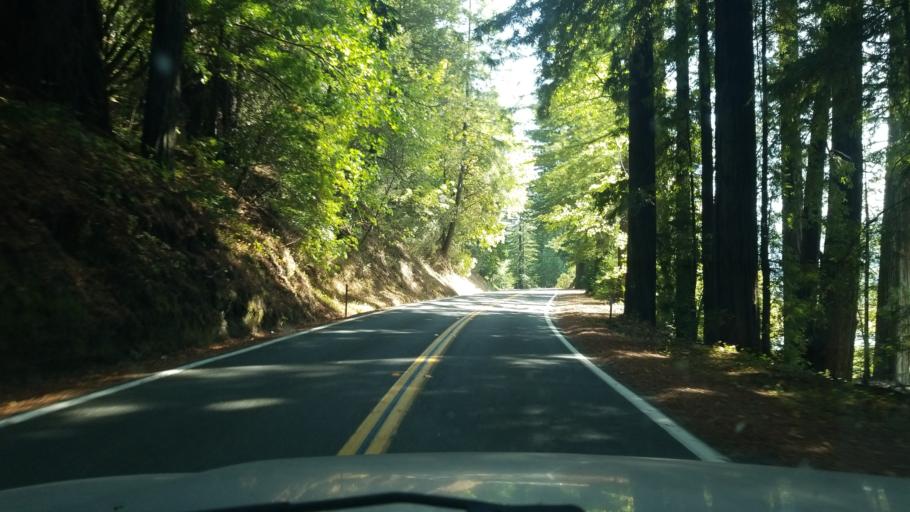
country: US
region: California
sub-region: Humboldt County
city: Redway
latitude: 40.2500
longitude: -123.8228
